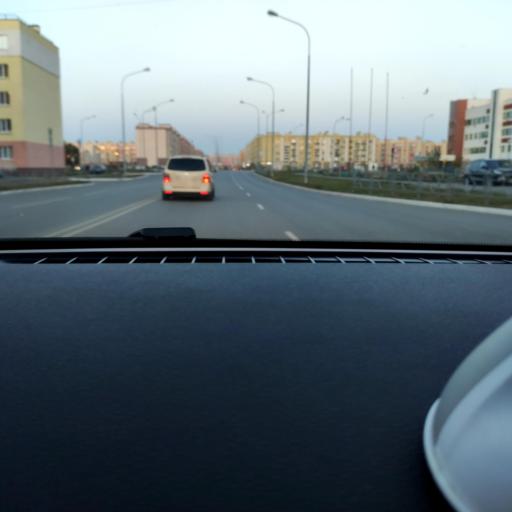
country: RU
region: Samara
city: Samara
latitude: 53.1151
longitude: 50.1520
